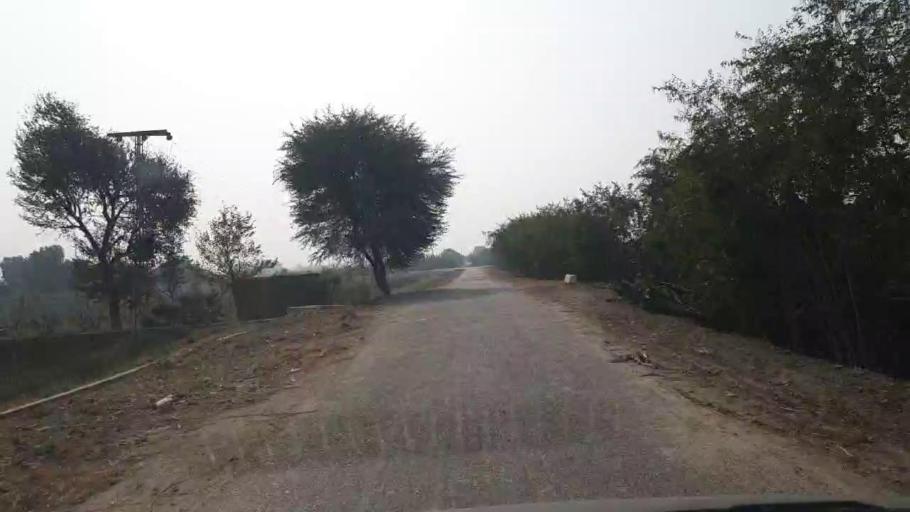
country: PK
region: Sindh
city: Hala
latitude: 25.8235
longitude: 68.4377
